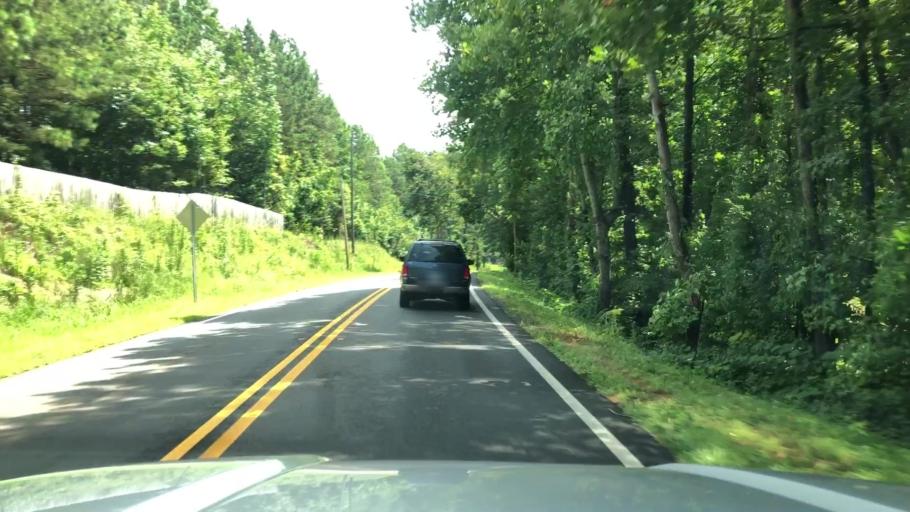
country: US
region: Georgia
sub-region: Bartow County
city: Emerson
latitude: 34.0771
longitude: -84.7778
